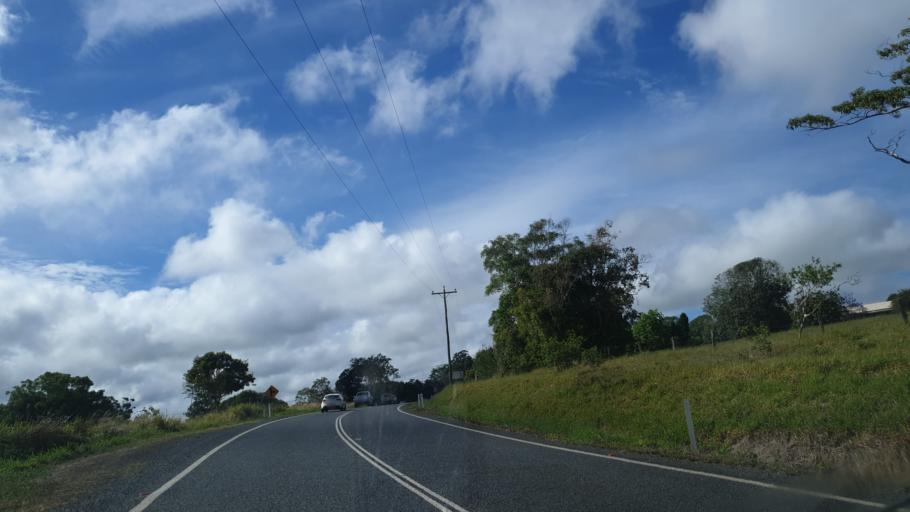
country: AU
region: Queensland
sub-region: Tablelands
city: Atherton
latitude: -17.3473
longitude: 145.5798
